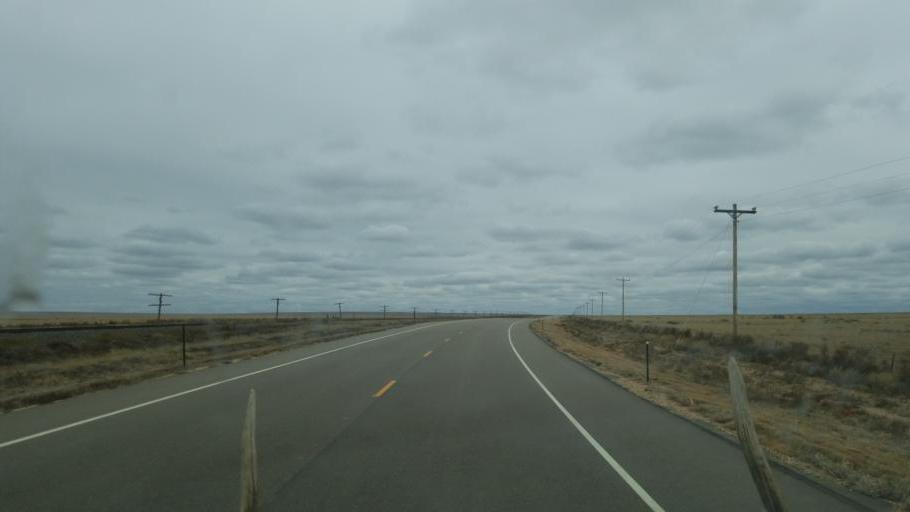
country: US
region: Colorado
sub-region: Bent County
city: Las Animas
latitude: 38.4056
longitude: -103.2961
